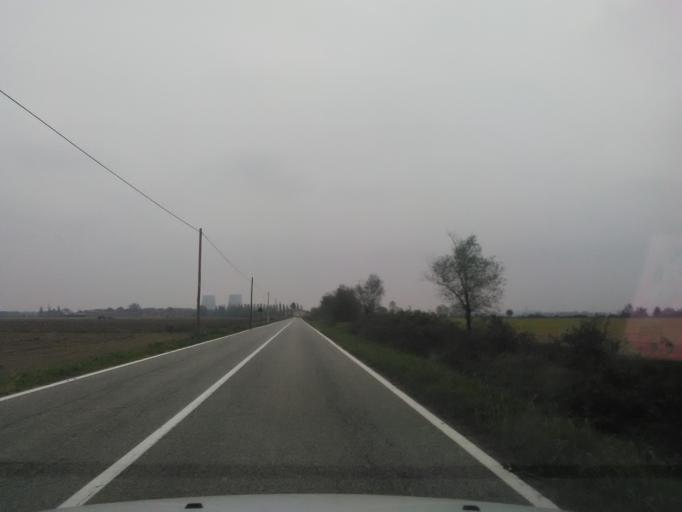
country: IT
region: Piedmont
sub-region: Provincia di Vercelli
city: Bianze
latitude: 45.2577
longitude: 8.1584
